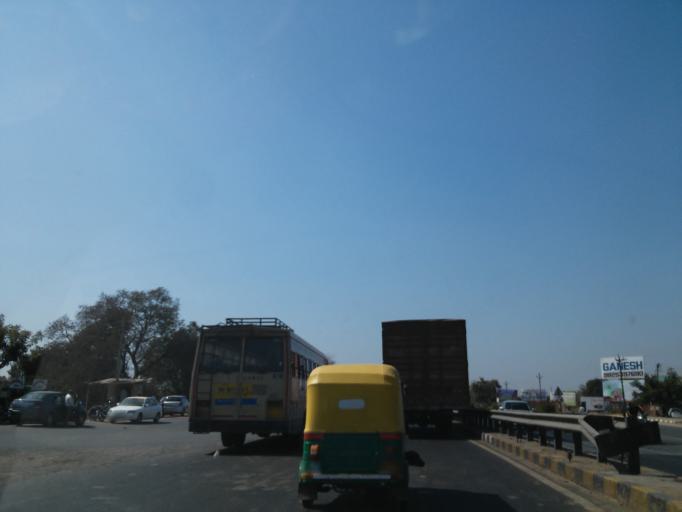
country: IN
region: Gujarat
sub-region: Mahesana
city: Vijapur
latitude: 23.4454
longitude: 72.8588
